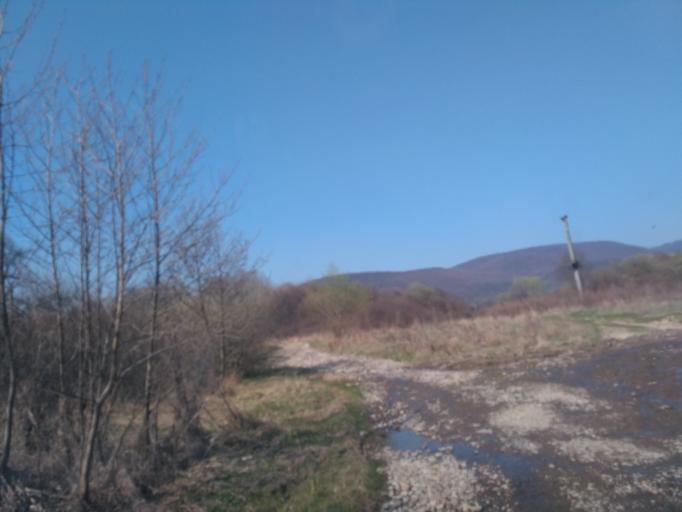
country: SK
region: Presovsky
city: Vranov nad Topl'ou
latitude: 48.8267
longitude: 21.6186
